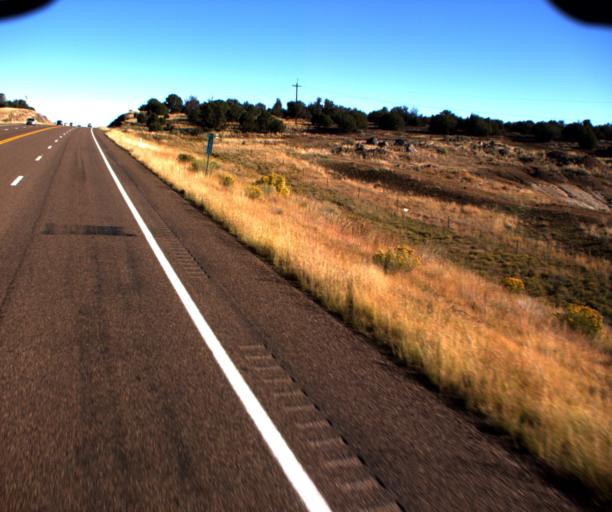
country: US
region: Arizona
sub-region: Navajo County
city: White Mountain Lake
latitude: 34.3638
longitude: -110.0524
